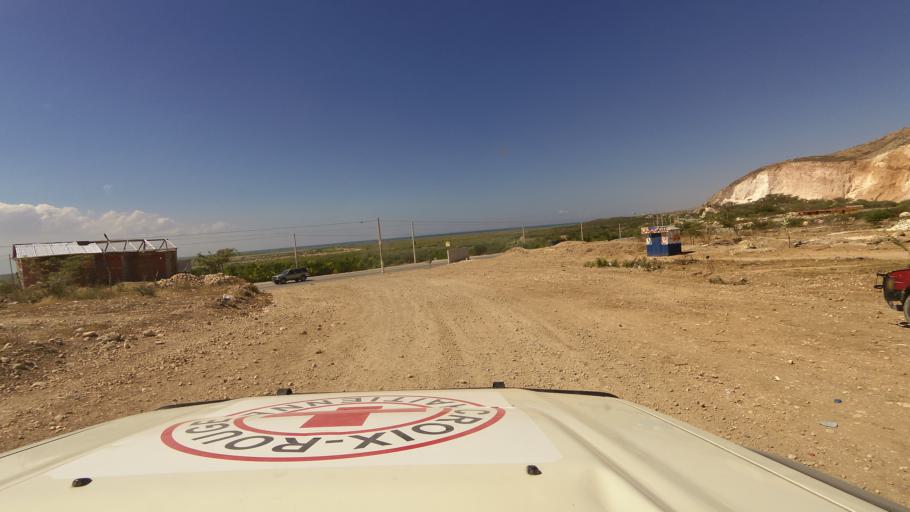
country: HT
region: Ouest
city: Croix des Bouquets
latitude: 18.6669
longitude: -72.2977
